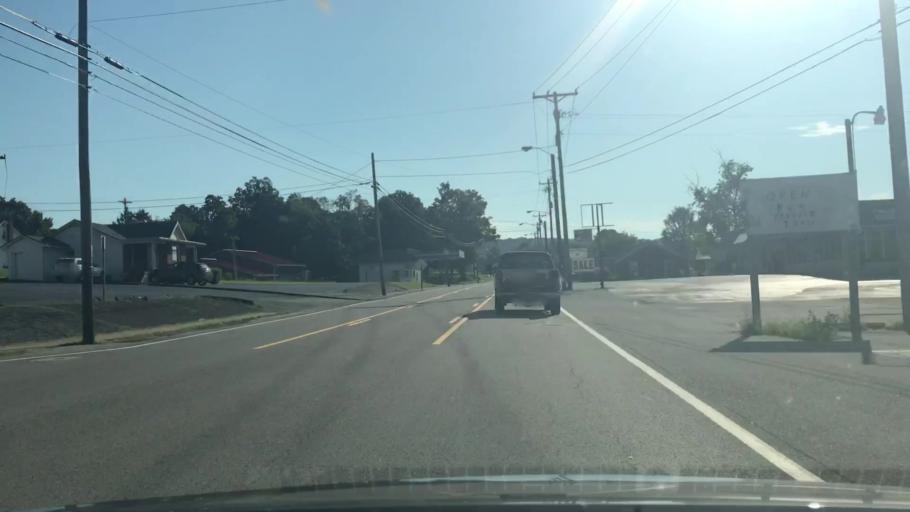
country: US
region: Tennessee
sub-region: Overton County
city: Livingston
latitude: 36.3875
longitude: -85.3129
